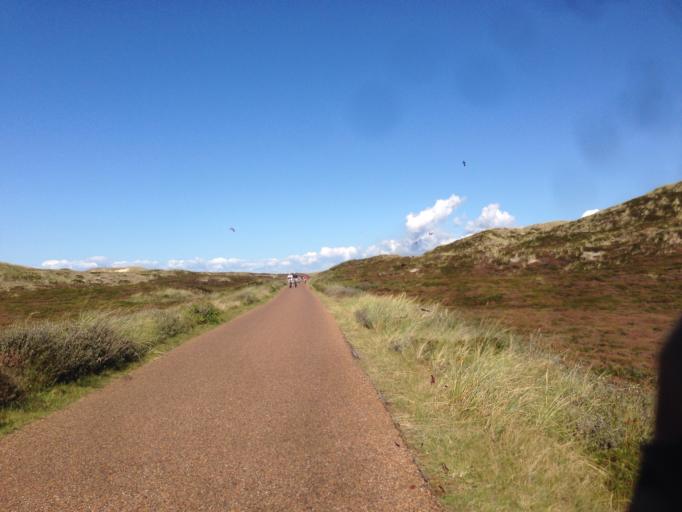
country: DE
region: Schleswig-Holstein
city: List
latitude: 54.9940
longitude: 8.3602
